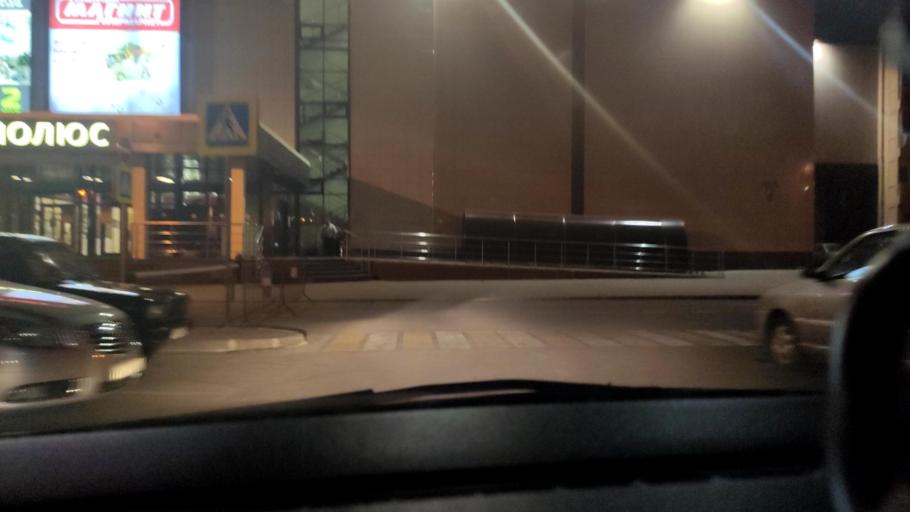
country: RU
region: Voronezj
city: Maslovka
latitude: 51.6025
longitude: 39.2382
